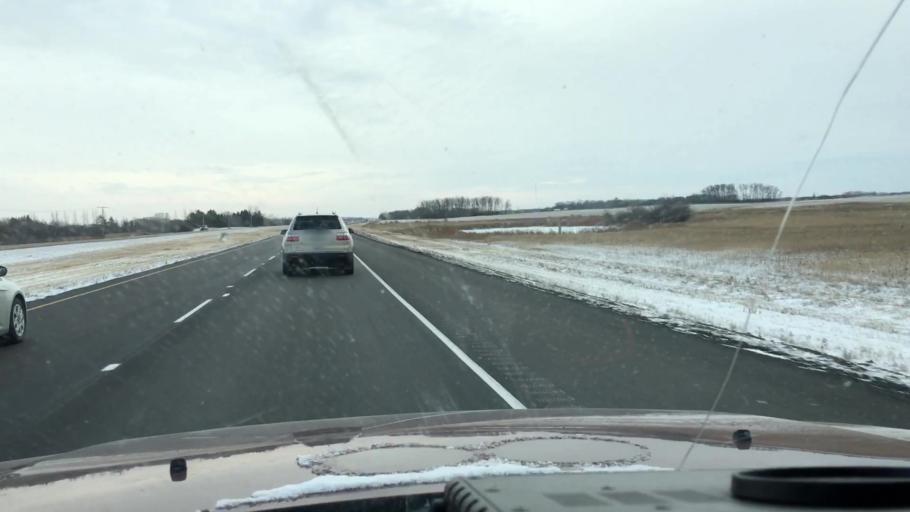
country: CA
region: Saskatchewan
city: Saskatoon
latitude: 52.0200
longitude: -106.5779
